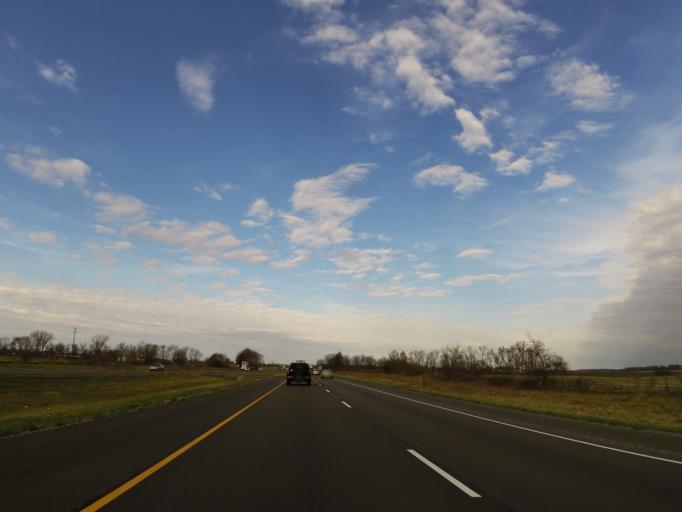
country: US
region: Illinois
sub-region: Washington County
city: Okawville
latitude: 38.4343
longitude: -89.5194
